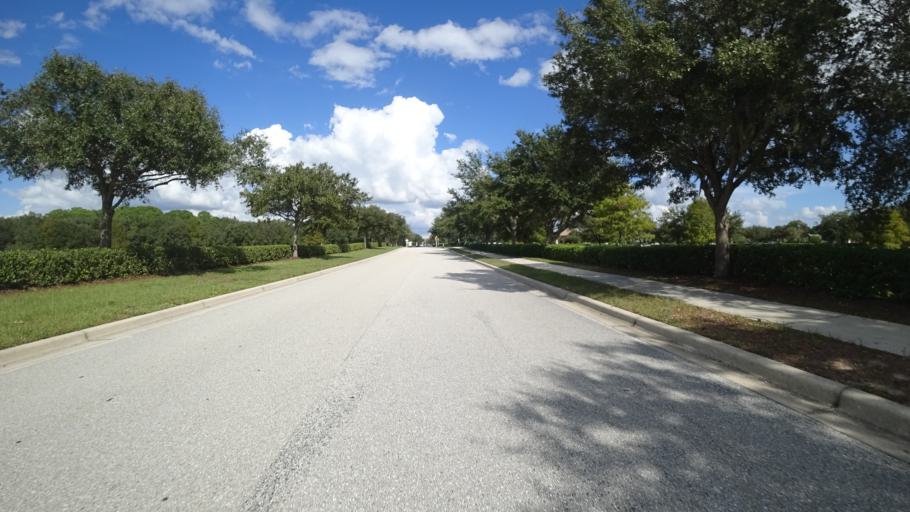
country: US
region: Florida
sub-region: Manatee County
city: Samoset
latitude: 27.4630
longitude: -82.4355
